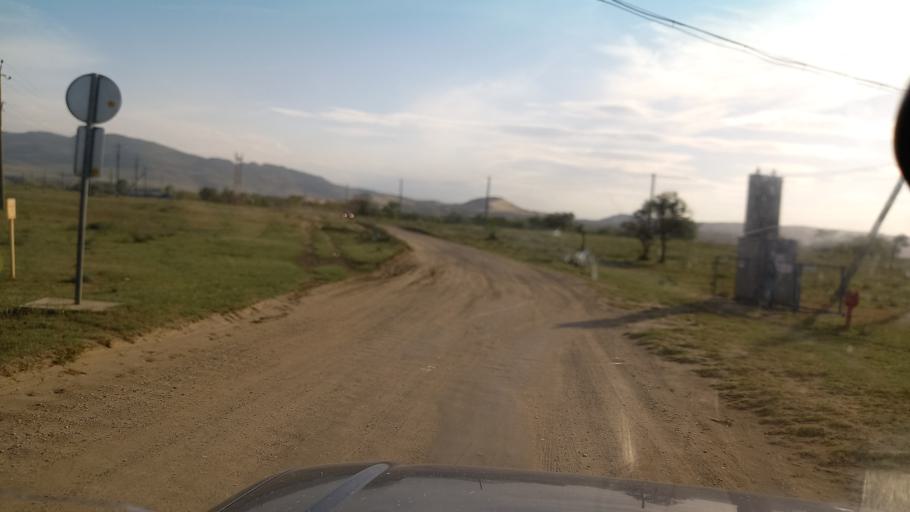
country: RU
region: Dagestan
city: Korkmaskala
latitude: 43.0240
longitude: 47.2638
